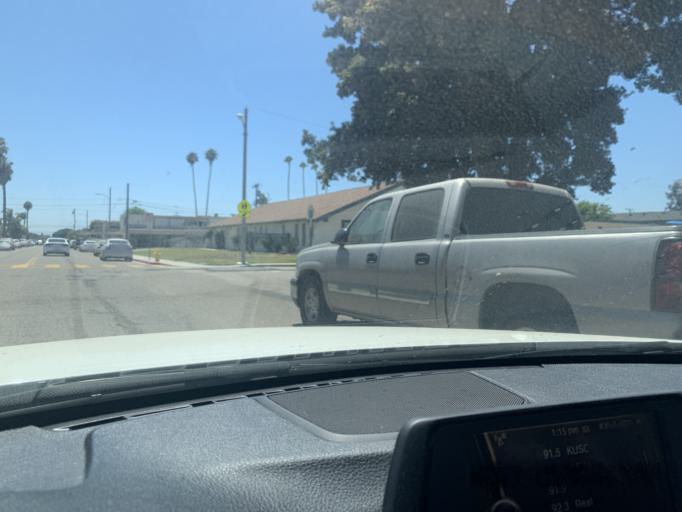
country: US
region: California
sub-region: Ventura County
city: Oxnard
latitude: 34.2139
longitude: -119.1923
